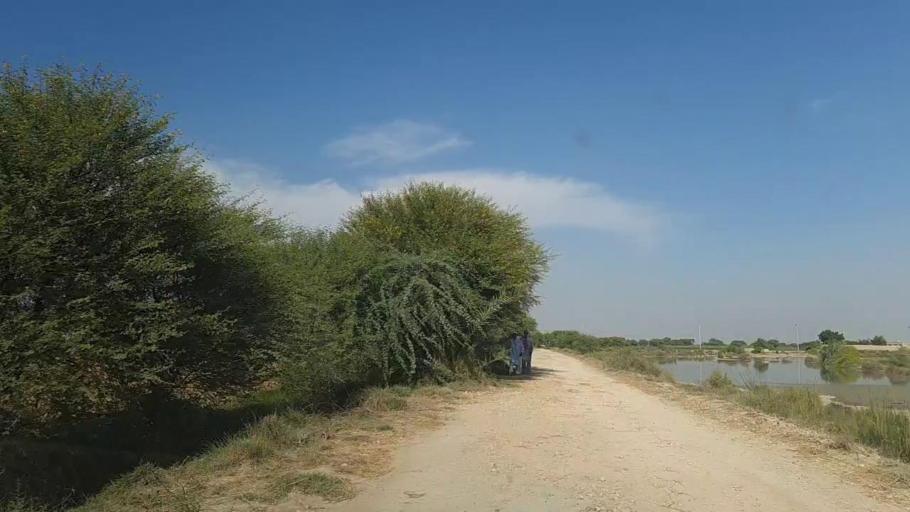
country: PK
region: Sindh
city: Bulri
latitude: 24.8630
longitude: 68.2612
